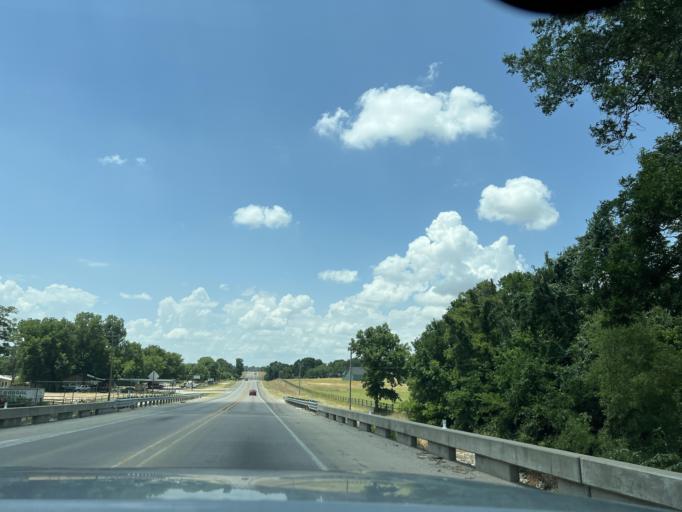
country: US
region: Texas
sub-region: Parker County
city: Weatherford
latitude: 32.8080
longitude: -97.7806
